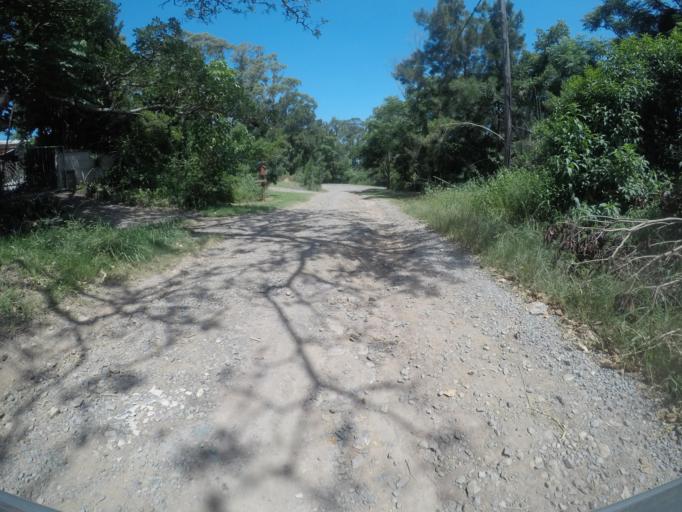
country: ZA
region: Eastern Cape
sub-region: Buffalo City Metropolitan Municipality
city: East London
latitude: -32.9696
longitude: 27.8557
